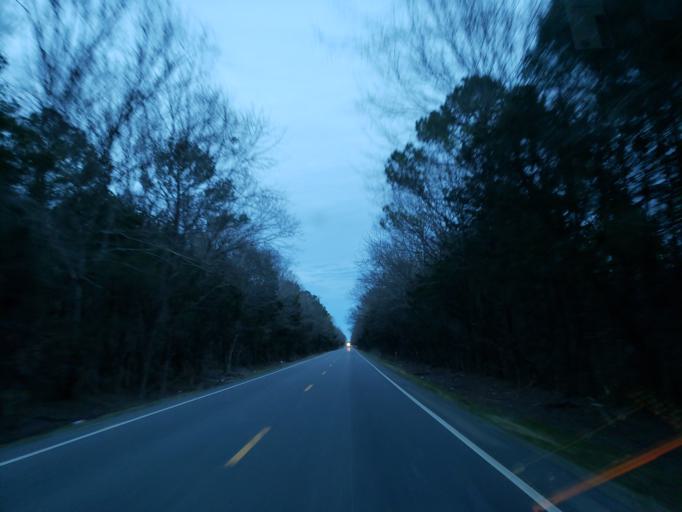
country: US
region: Alabama
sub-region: Sumter County
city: Livingston
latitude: 32.8109
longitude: -88.2420
